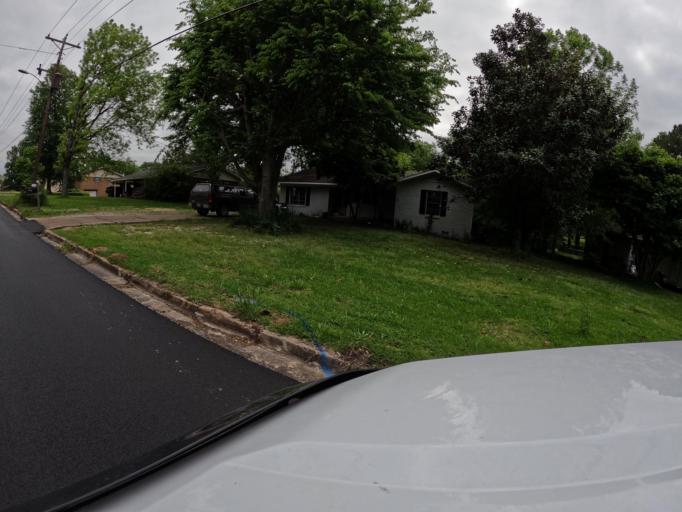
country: US
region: Mississippi
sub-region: Lee County
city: Tupelo
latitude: 34.2615
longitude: -88.7464
